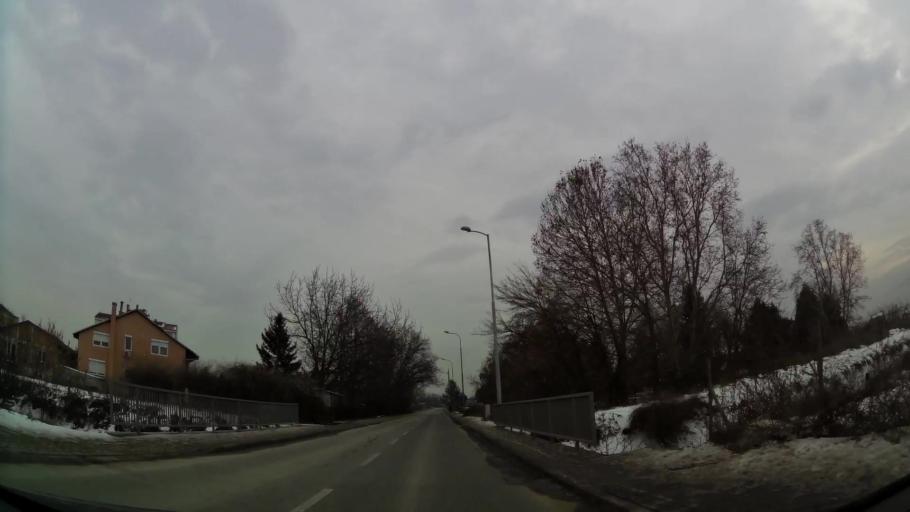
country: MK
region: Butel
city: Butel
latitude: 42.0370
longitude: 21.4431
